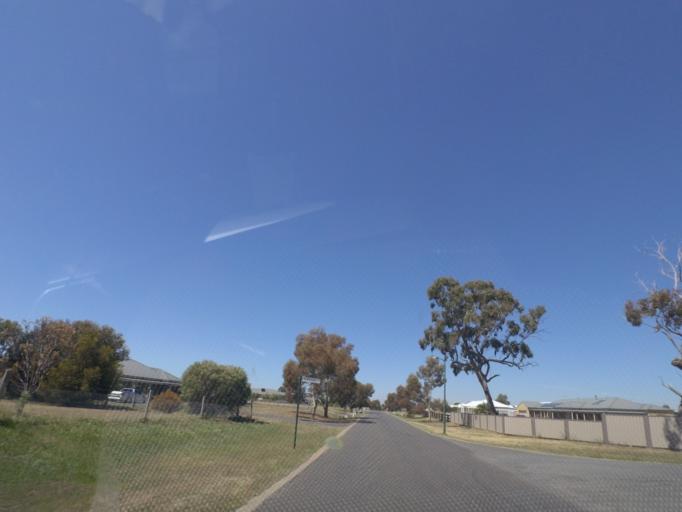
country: AU
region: Victoria
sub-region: Melton
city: Brookfield
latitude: -37.7017
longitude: 144.5019
